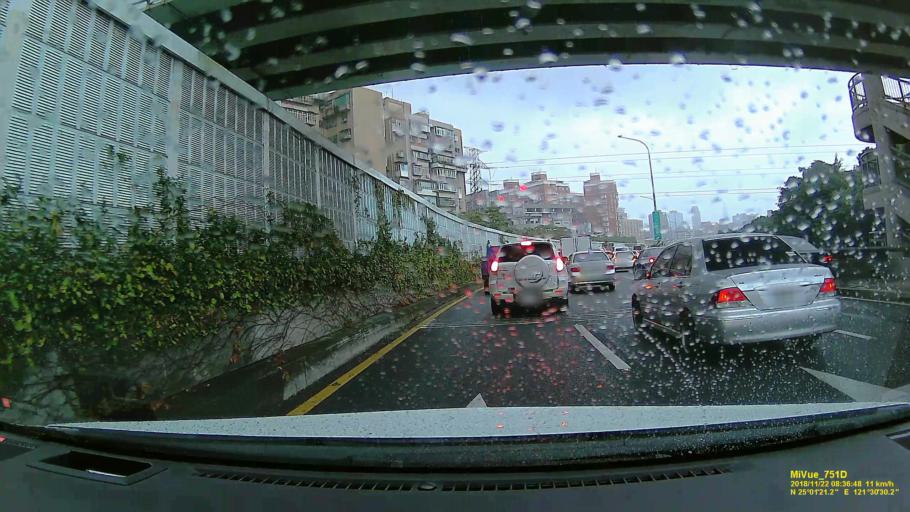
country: TW
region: Taipei
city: Taipei
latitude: 25.0226
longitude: 121.5085
